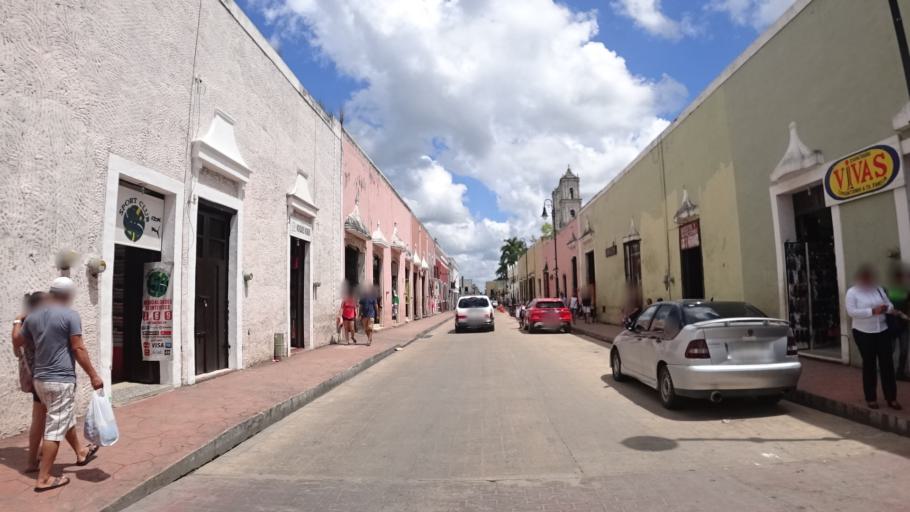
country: MX
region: Yucatan
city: Valladolid
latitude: 20.6897
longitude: -88.2033
